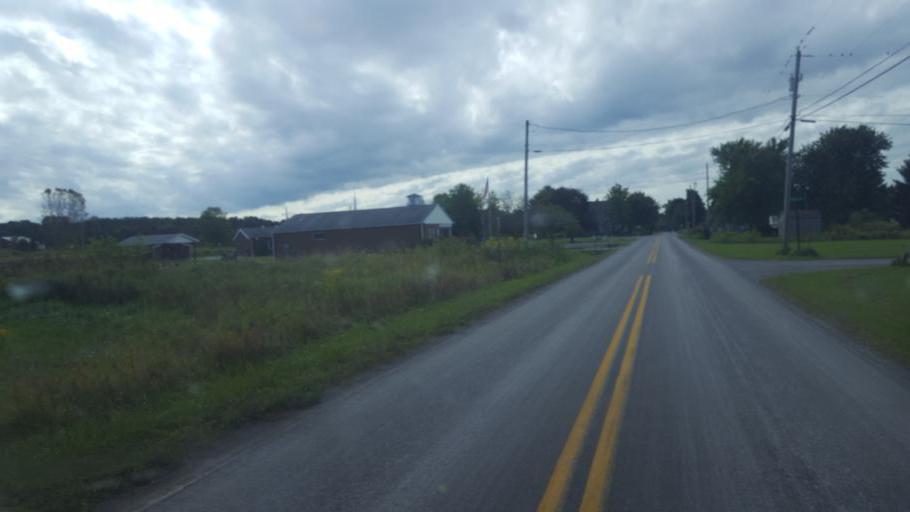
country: US
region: Pennsylvania
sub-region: Mercer County
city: Greenville
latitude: 41.5061
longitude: -80.3379
